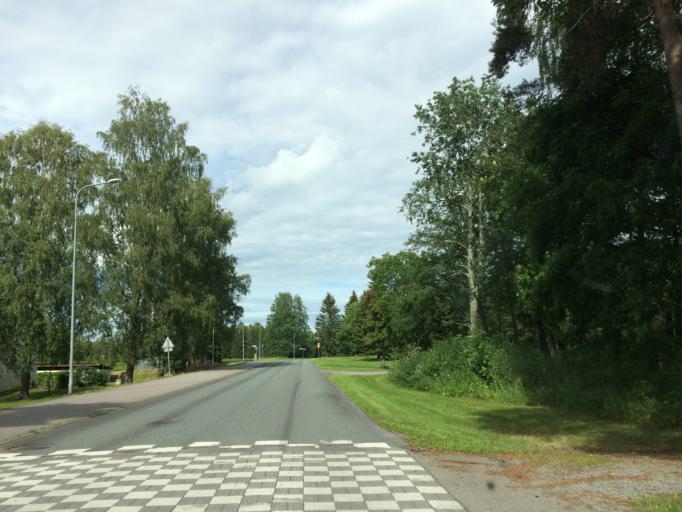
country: FI
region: Haeme
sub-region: Haemeenlinna
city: Turenki
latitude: 60.9279
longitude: 24.6516
